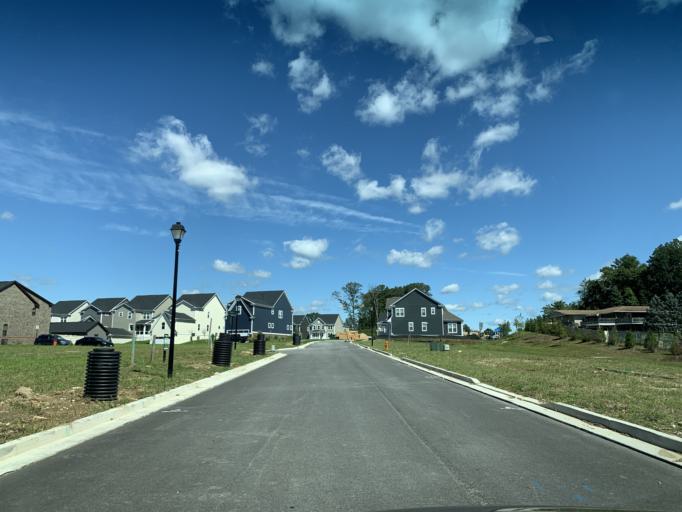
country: US
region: Maryland
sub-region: Baltimore County
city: Bowleys Quarters
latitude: 39.3579
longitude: -76.3998
